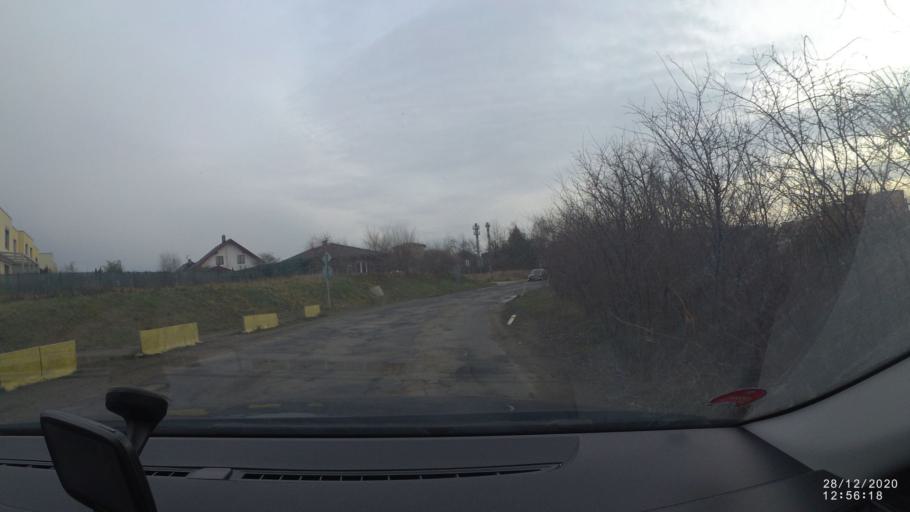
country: CZ
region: Praha
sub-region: Praha 19
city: Satalice
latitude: 50.1541
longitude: 14.5837
